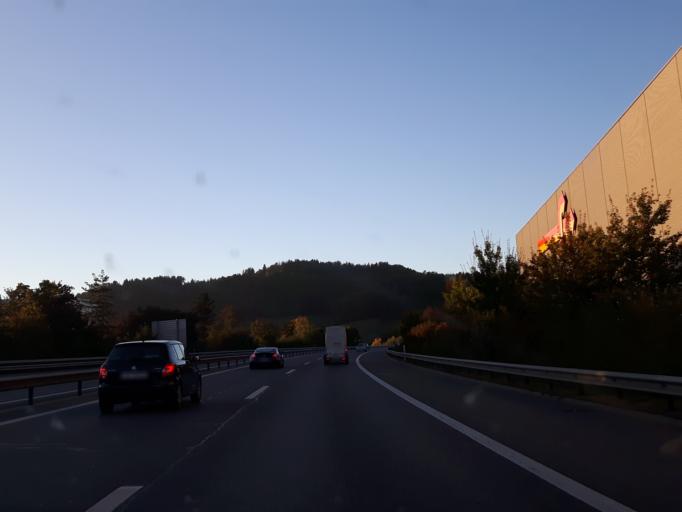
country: CH
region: Lucerne
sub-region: Willisau District
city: Dagmersellen
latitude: 47.2106
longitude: 7.9801
